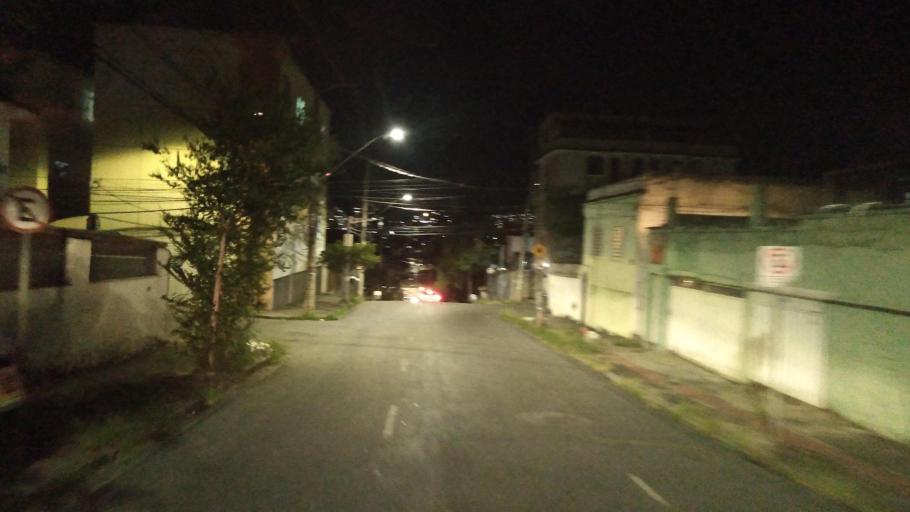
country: BR
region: Minas Gerais
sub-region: Belo Horizonte
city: Belo Horizonte
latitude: -19.9081
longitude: -43.9166
